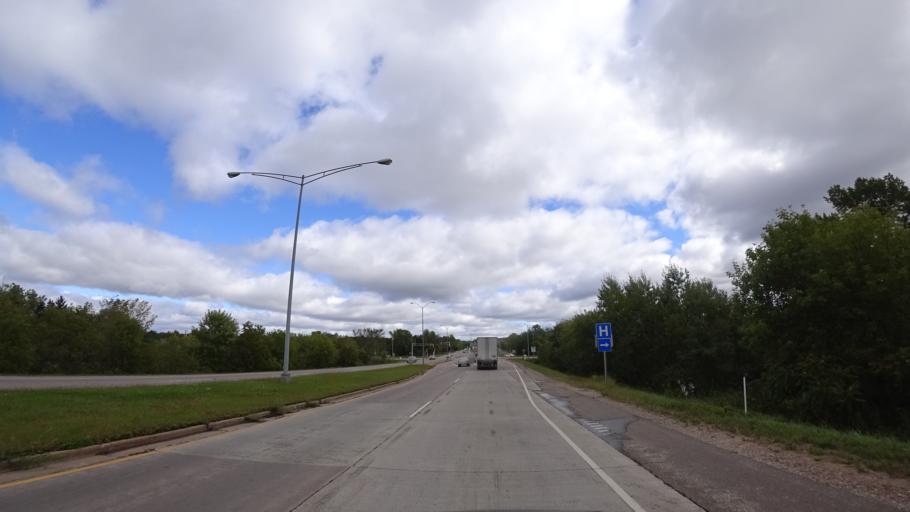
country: US
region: Wisconsin
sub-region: Eau Claire County
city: Eau Claire
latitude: 44.8411
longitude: -91.5096
